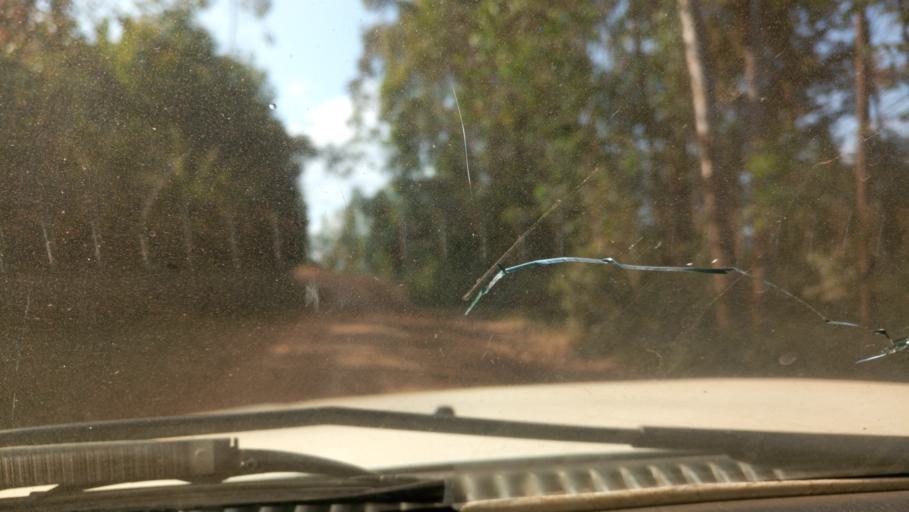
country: KE
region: Murang'a District
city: Kangema
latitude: -0.8276
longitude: 36.9826
